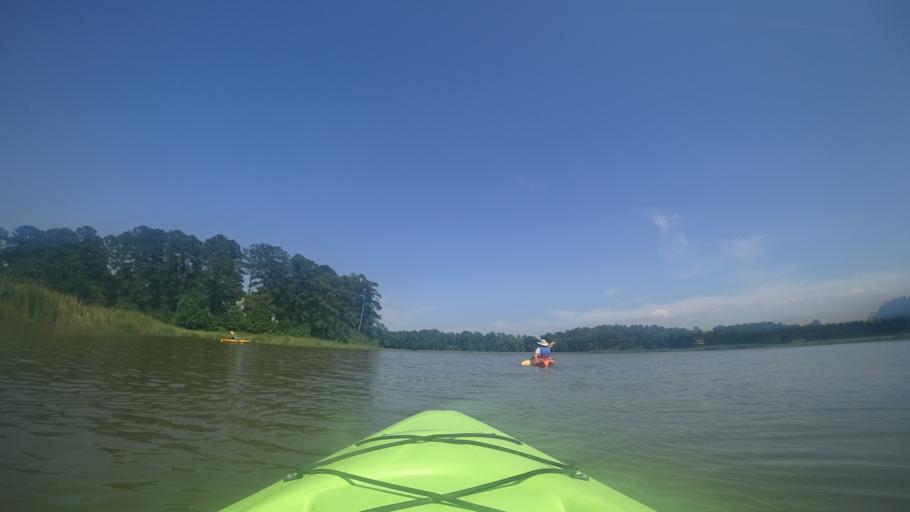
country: US
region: Virginia
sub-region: Isle of Wight County
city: Smithfield
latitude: 36.9613
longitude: -76.6165
